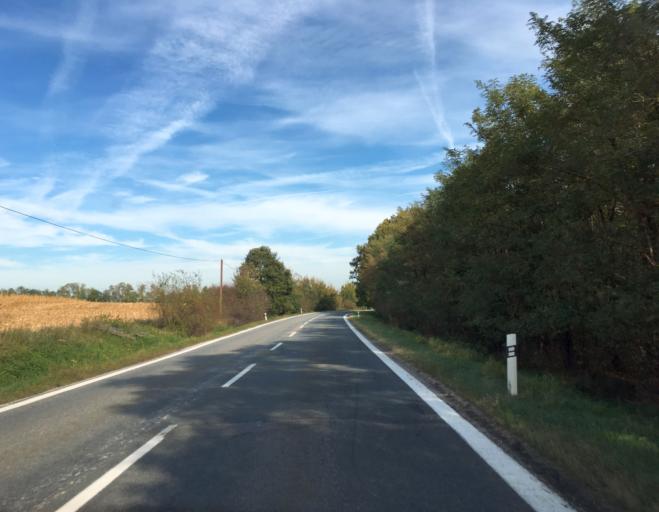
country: SK
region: Nitriansky
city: Svodin
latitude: 48.0358
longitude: 18.4241
